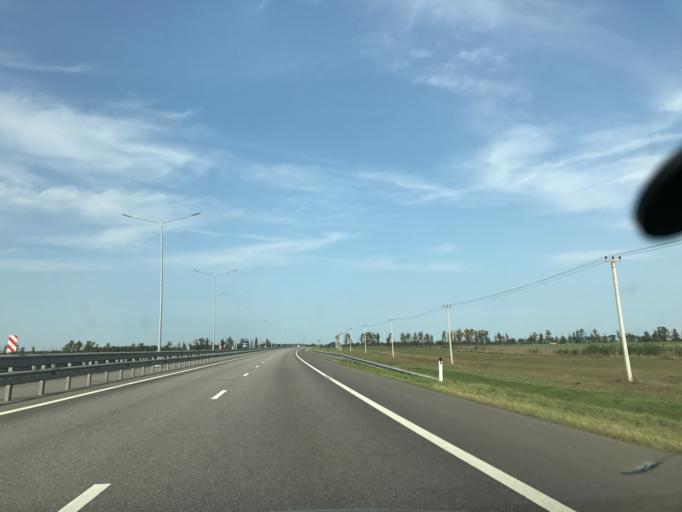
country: RU
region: Voronezj
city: Podkletnoye
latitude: 51.5176
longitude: 39.5113
